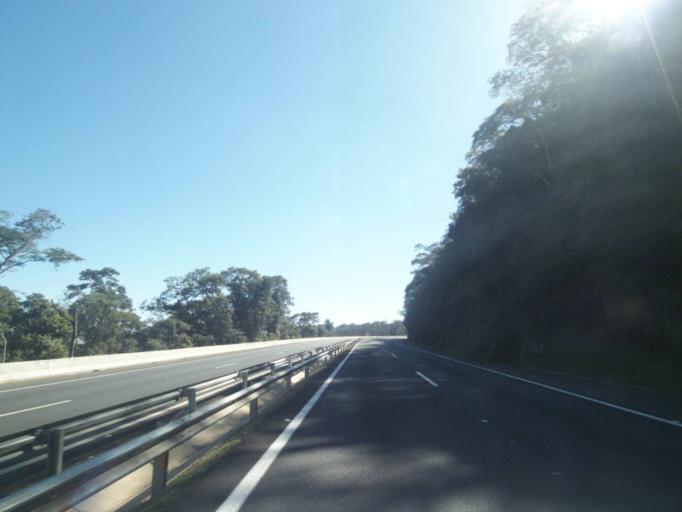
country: BR
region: Parana
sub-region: Tibagi
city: Tibagi
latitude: -24.8121
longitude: -50.4893
